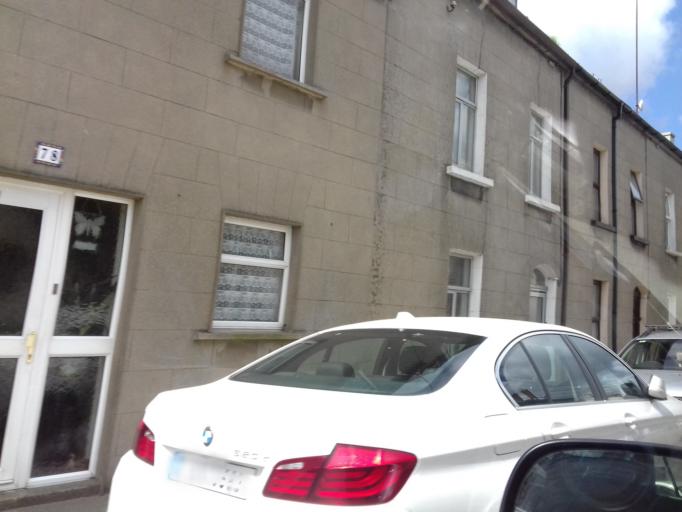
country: IE
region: Leinster
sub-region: Loch Garman
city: Loch Garman
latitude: 52.3316
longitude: -6.4553
